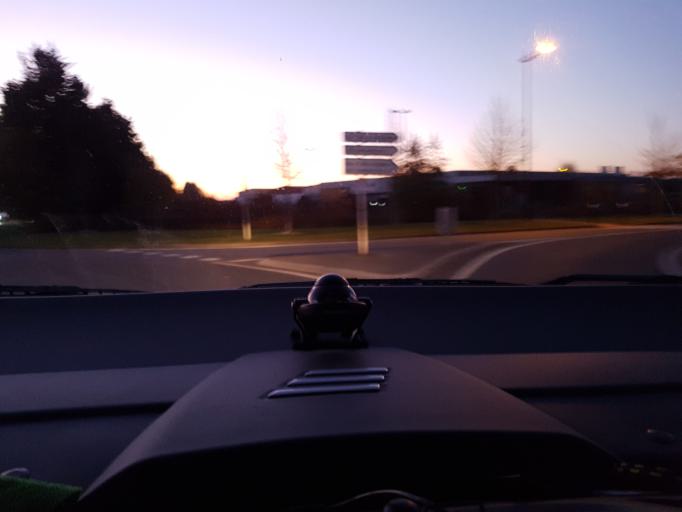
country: FR
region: Picardie
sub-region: Departement de la Somme
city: Saint-Valery-sur-Somme
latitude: 50.1732
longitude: 1.6364
